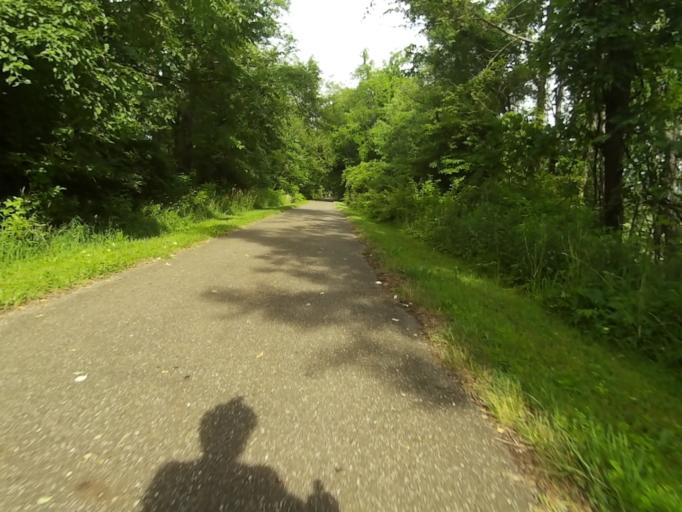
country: US
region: Ohio
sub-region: Portage County
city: Kent
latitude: 41.1856
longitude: -81.3710
